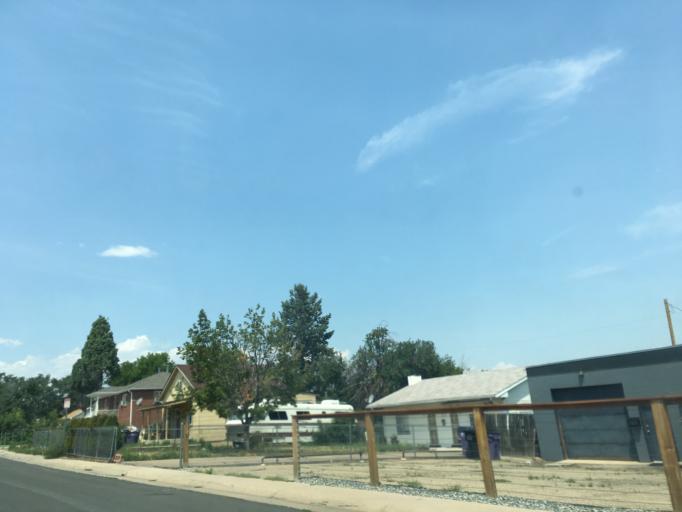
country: US
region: Colorado
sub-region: Jefferson County
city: Lakewood
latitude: 39.7058
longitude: -105.0299
